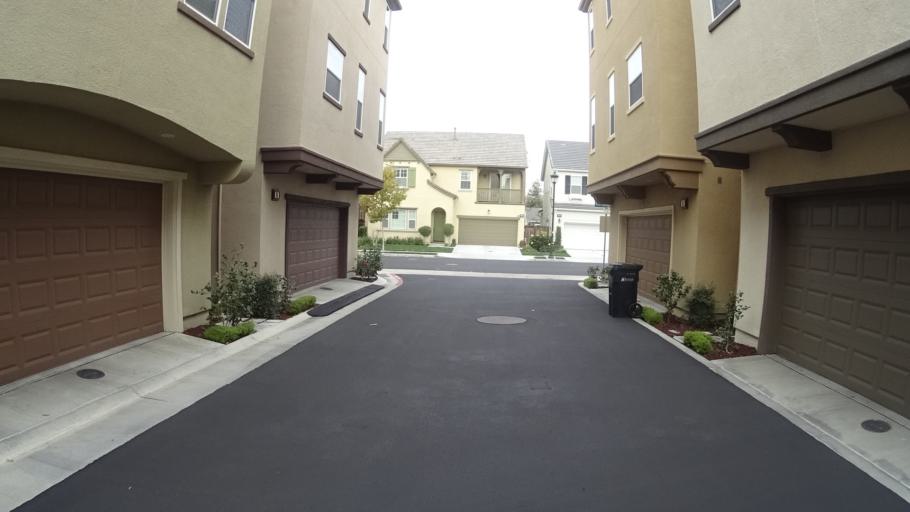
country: US
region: California
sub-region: Santa Clara County
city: Burbank
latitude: 37.3265
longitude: -121.9531
